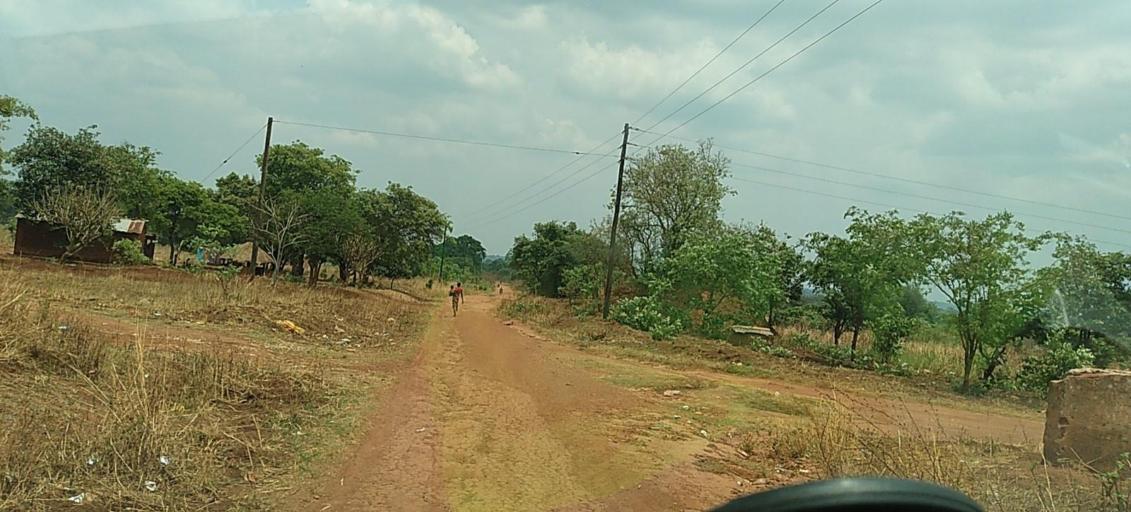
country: ZM
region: North-Western
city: Kansanshi
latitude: -12.0368
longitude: 26.4013
